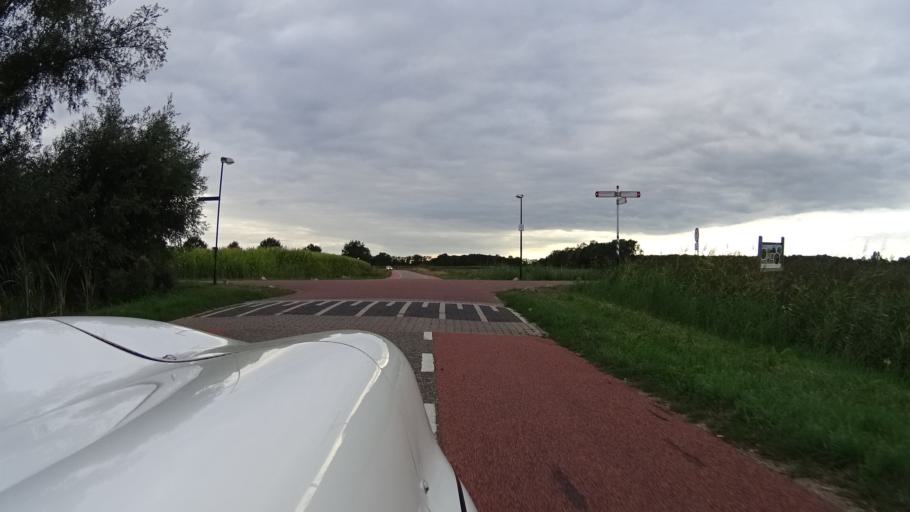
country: NL
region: North Brabant
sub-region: Gemeente Bernheze
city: Loosbroek
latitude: 51.6905
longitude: 5.4800
